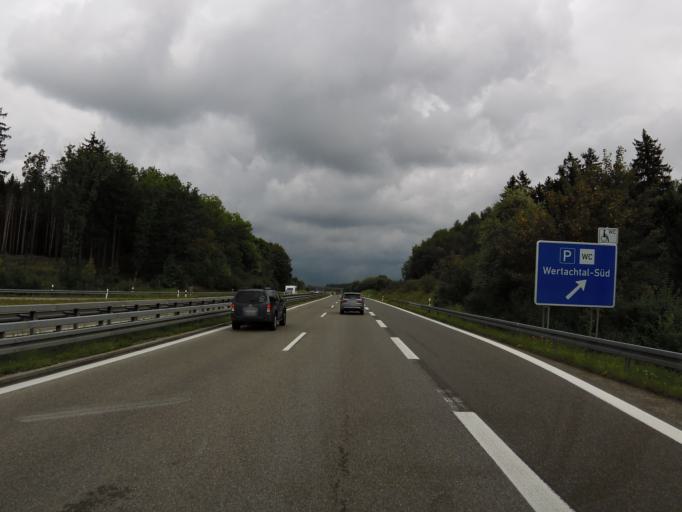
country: DE
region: Bavaria
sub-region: Swabia
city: Wiedergeltingen
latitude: 48.0304
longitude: 10.6661
